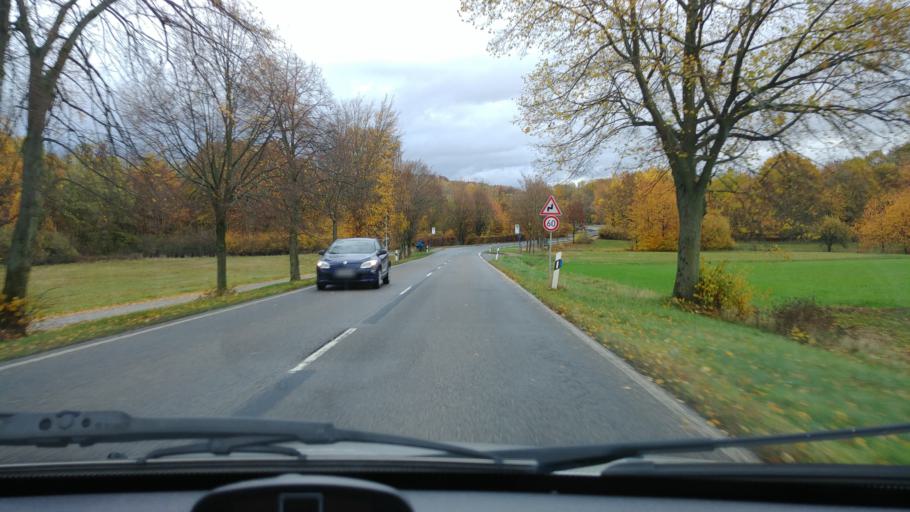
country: DE
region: Hesse
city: Mengerskirchen
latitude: 50.5436
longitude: 8.1483
